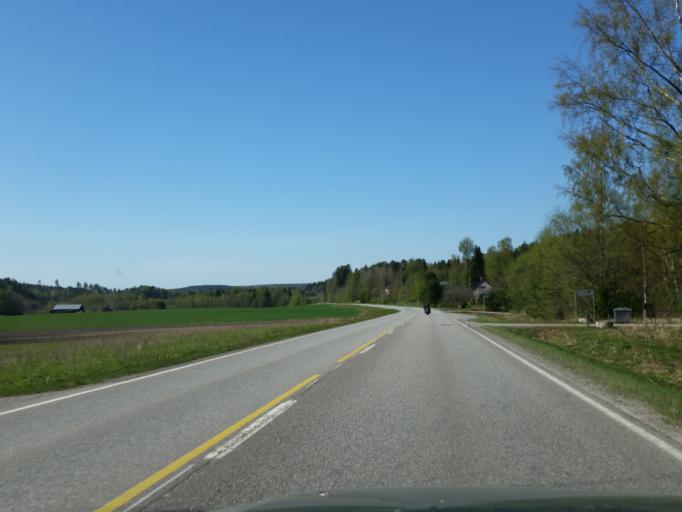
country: FI
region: Uusimaa
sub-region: Helsinki
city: Siuntio
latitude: 60.1848
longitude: 24.2405
